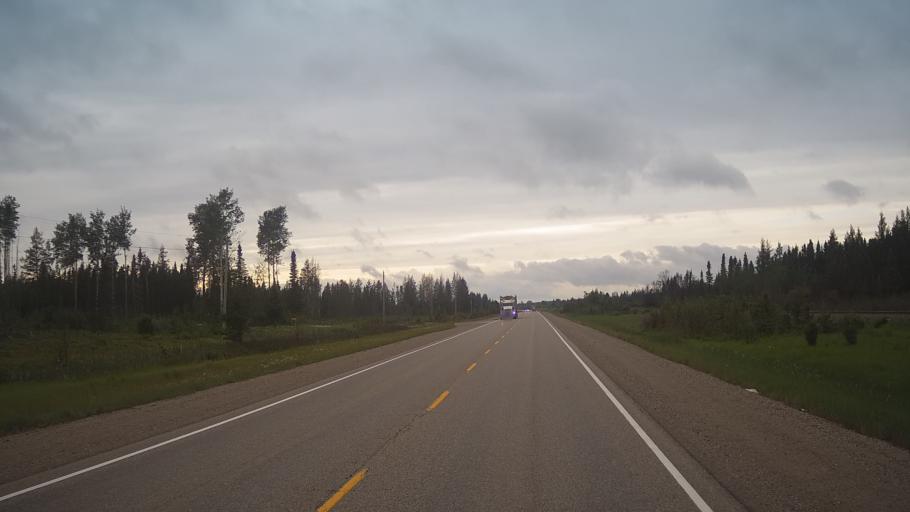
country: CA
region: Ontario
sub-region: Thunder Bay District
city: Thunder Bay
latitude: 48.8683
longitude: -89.9727
